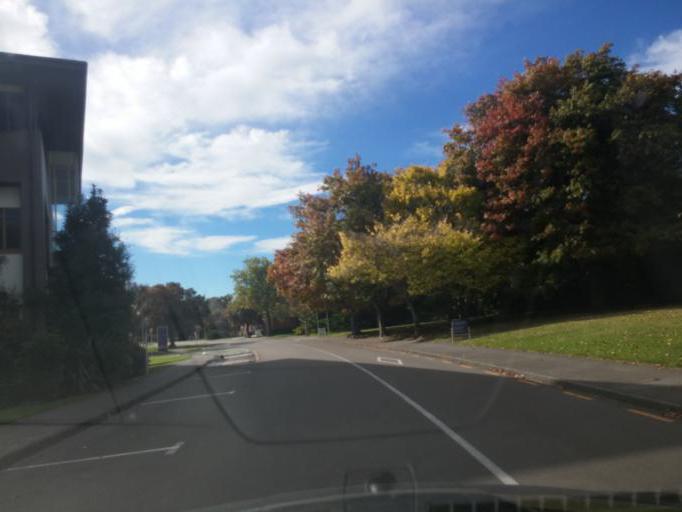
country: NZ
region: Manawatu-Wanganui
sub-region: Palmerston North City
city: Palmerston North
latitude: -40.3888
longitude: 175.6188
